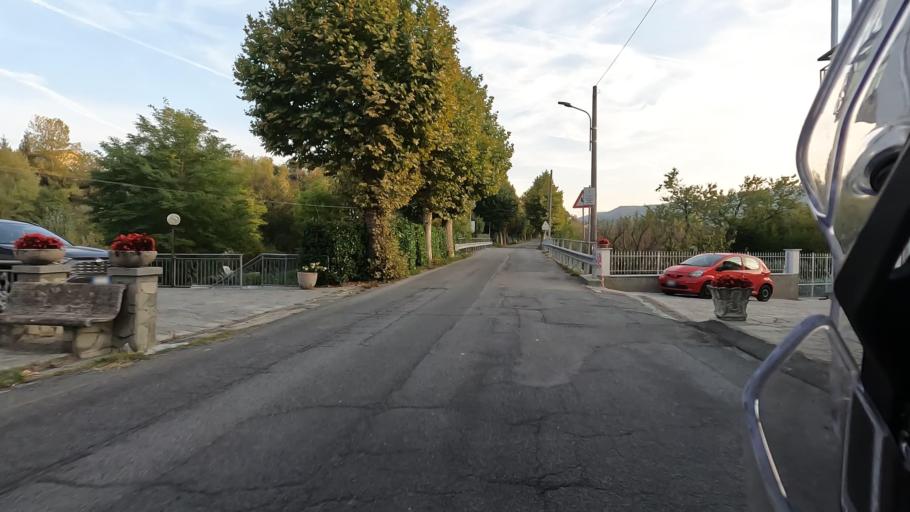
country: IT
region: Liguria
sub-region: Provincia di Savona
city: Mioglia
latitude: 44.4879
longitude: 8.4110
